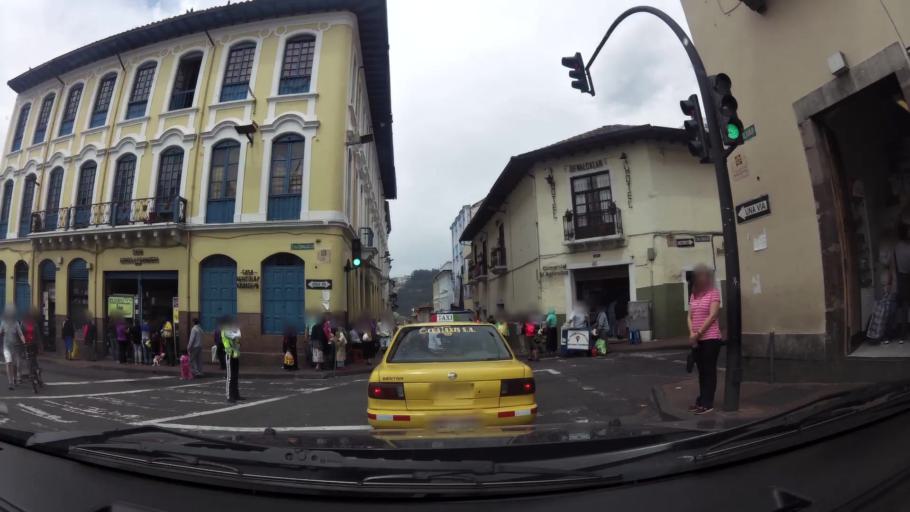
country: EC
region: Pichincha
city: Quito
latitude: -0.2213
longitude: -78.5151
